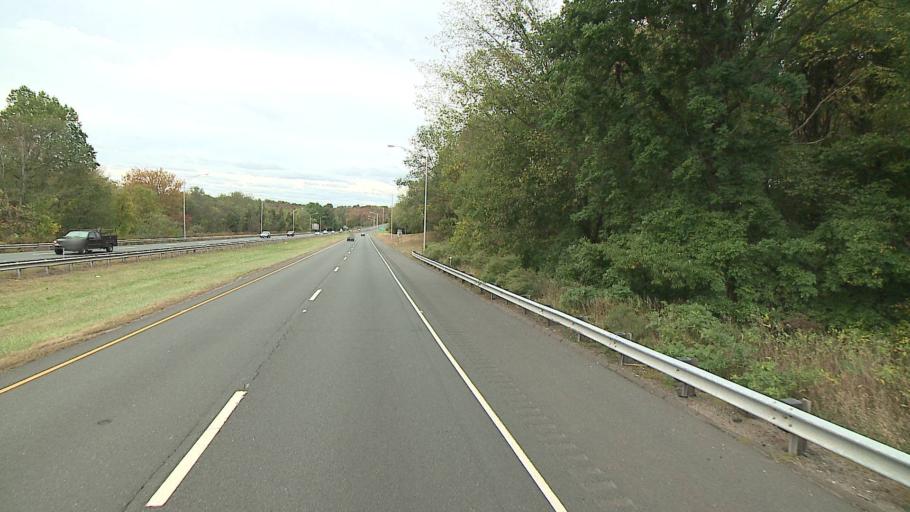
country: US
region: Connecticut
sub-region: Middlesex County
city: Middletown
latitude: 41.5368
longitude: -72.6205
